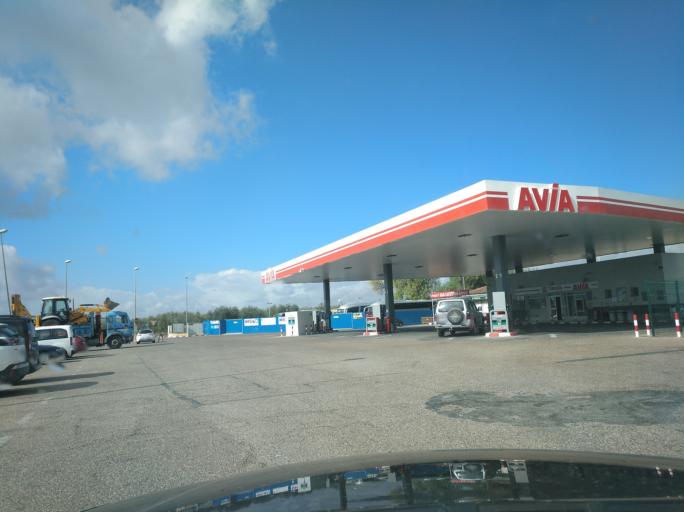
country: ES
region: Andalusia
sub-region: Provincia de Sevilla
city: Umbrete
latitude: 37.3624
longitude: -6.1440
